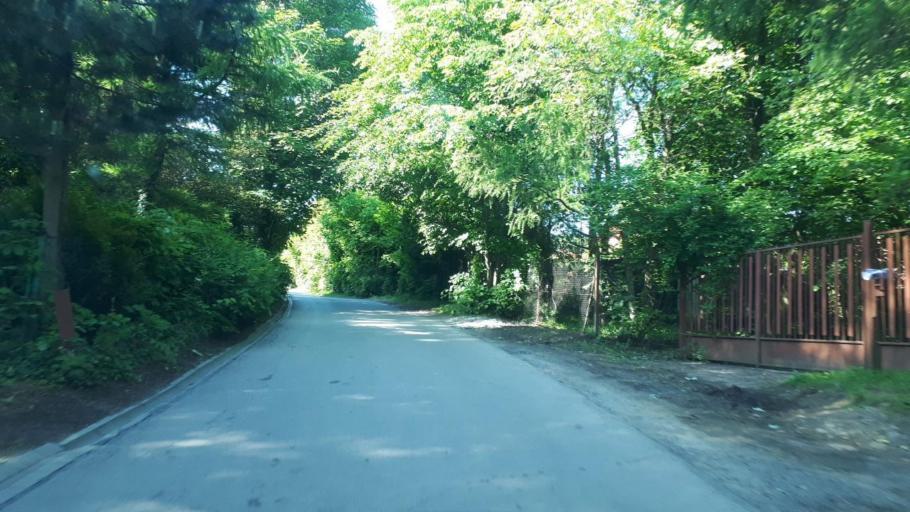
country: PL
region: Silesian Voivodeship
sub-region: Powiat bielski
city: Jaworze
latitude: 49.7890
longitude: 18.9450
